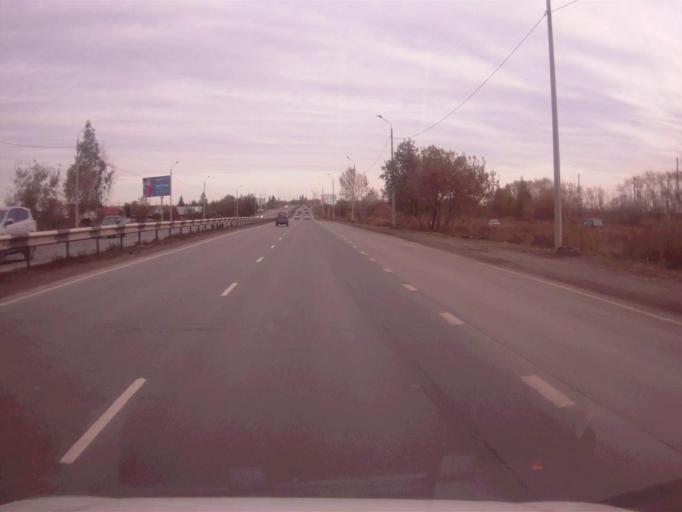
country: RU
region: Chelyabinsk
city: Novosineglazovskiy
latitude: 55.0420
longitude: 61.4305
